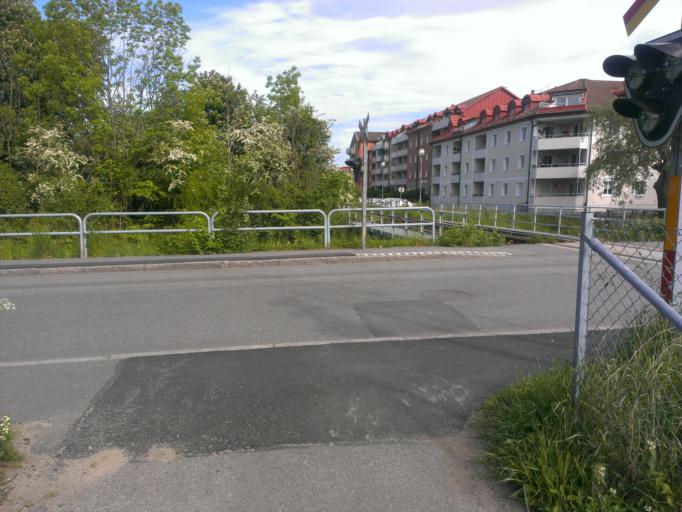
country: SE
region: Skane
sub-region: Kristianstads Kommun
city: Kristianstad
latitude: 56.0241
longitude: 14.1594
